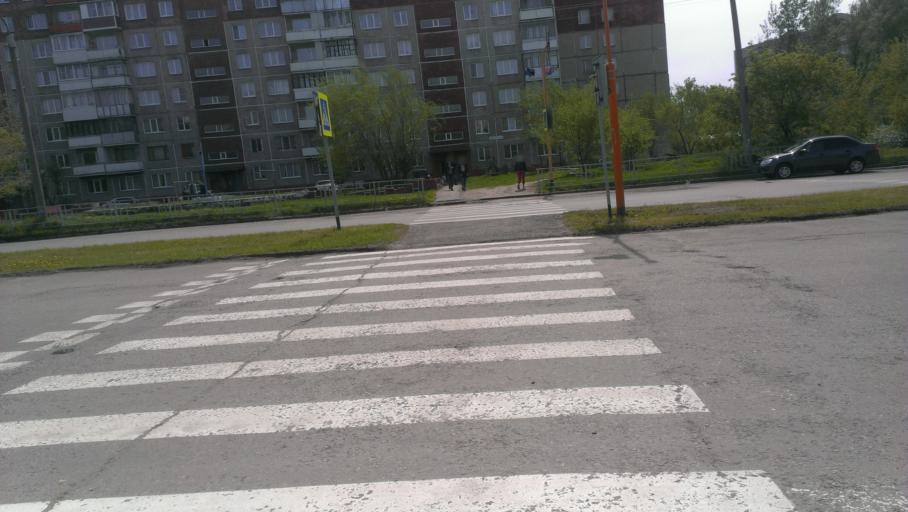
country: RU
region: Altai Krai
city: Novosilikatnyy
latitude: 53.3628
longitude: 83.6684
